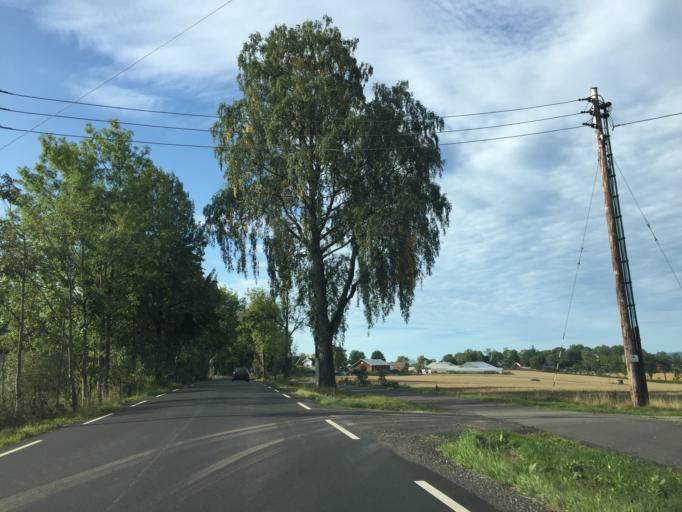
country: NO
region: Akershus
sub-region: As
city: As
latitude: 59.7103
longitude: 10.7722
